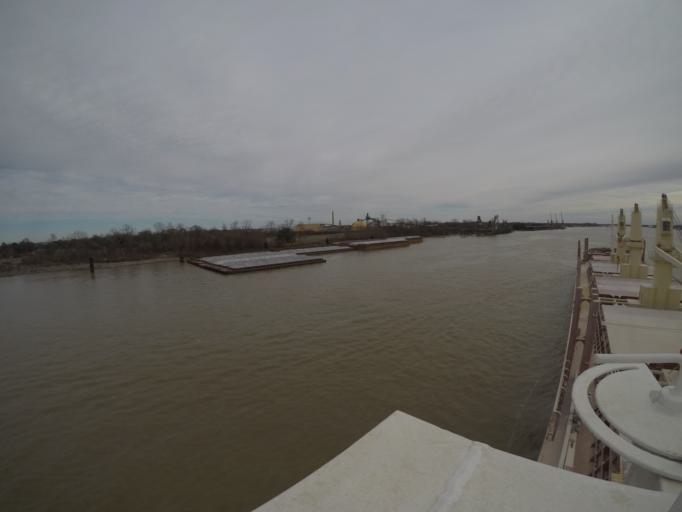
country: US
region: Louisiana
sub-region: Saint John the Baptist Parish
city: Edgard
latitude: 30.0530
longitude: -90.5754
